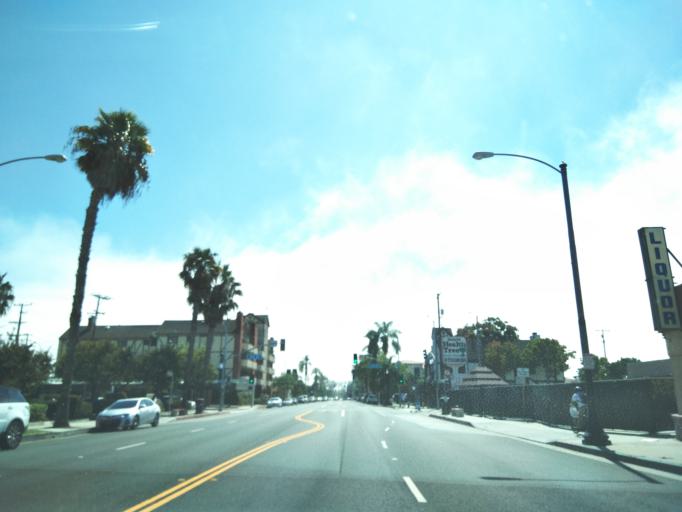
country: US
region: California
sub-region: Los Angeles County
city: Long Beach
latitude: 33.7686
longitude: -118.1525
